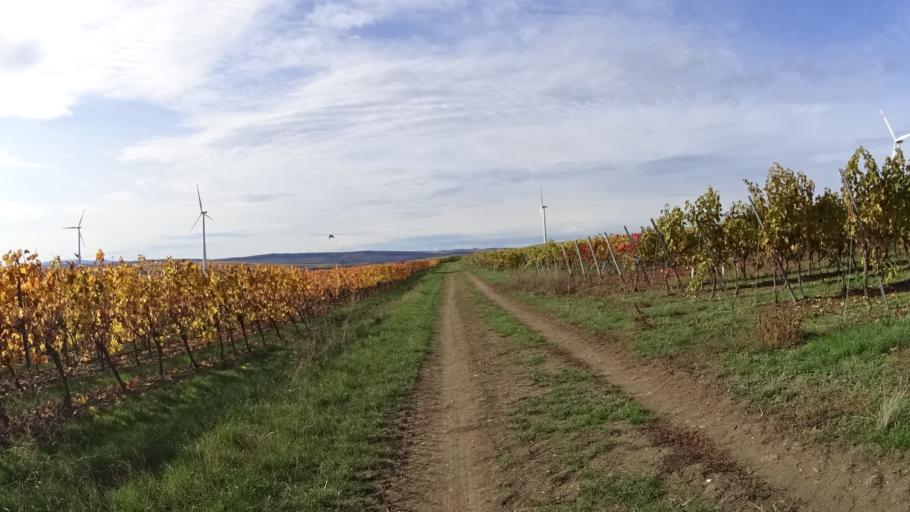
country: DE
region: Rheinland-Pfalz
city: Gau-Bickelheim
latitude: 49.8099
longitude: 8.0163
